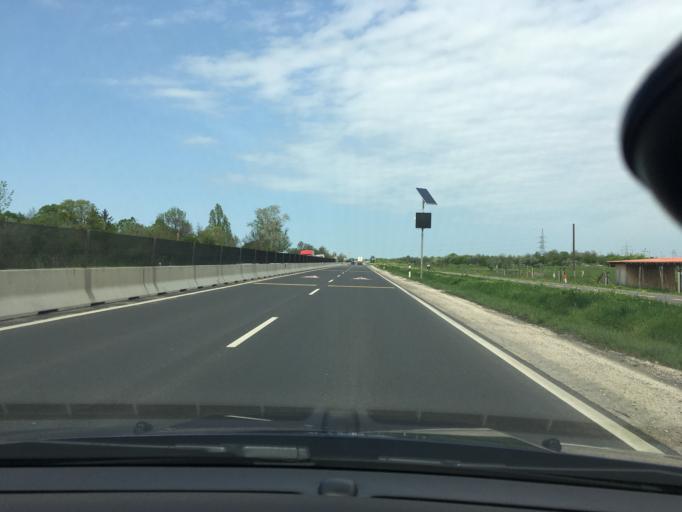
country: HU
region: Csongrad
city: Algyo
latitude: 46.2995
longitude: 20.1792
